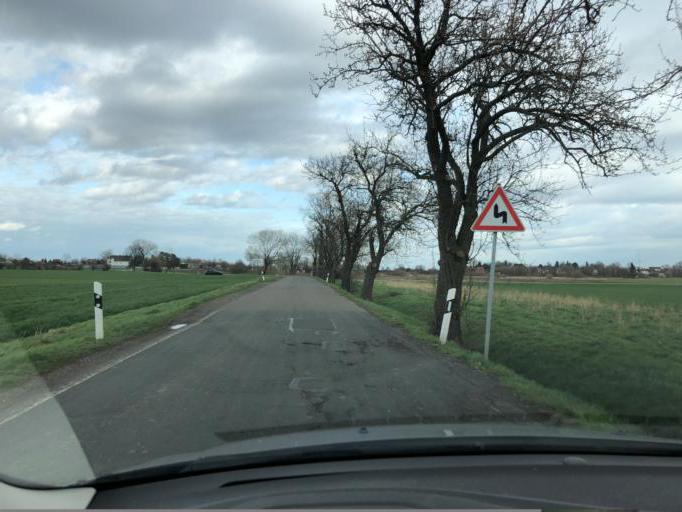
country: DE
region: Saxony
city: Markranstadt
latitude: 51.2769
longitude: 12.2195
